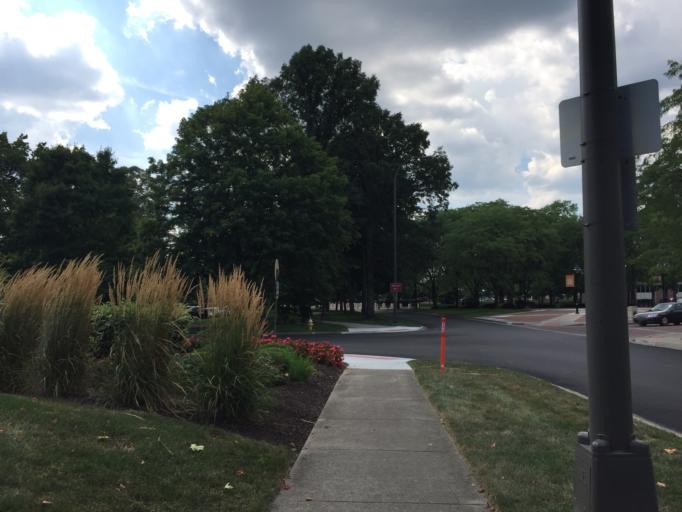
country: US
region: Ohio
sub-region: Montgomery County
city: Kettering
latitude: 39.6968
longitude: -84.1608
